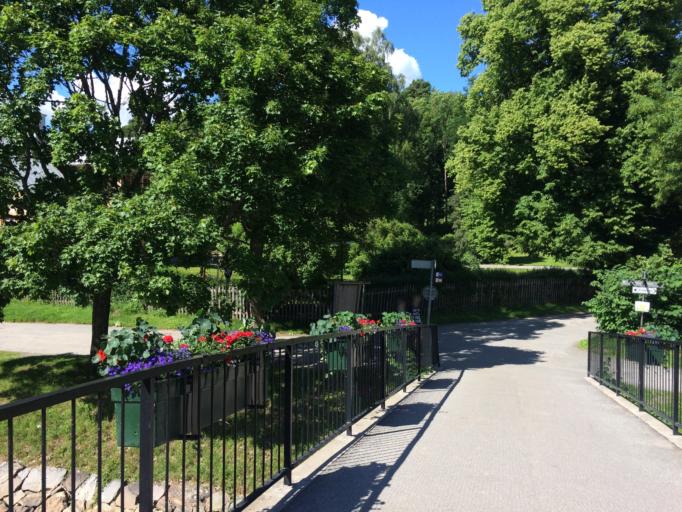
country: SE
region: Stockholm
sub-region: Nacka Kommun
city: Nacka
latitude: 59.3266
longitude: 18.1470
